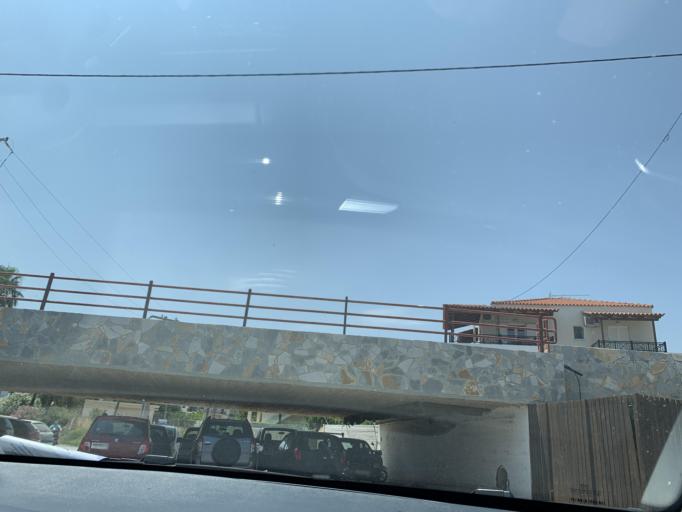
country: GR
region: Crete
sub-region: Nomos Chanias
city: Kalivai
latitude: 35.4485
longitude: 24.2011
